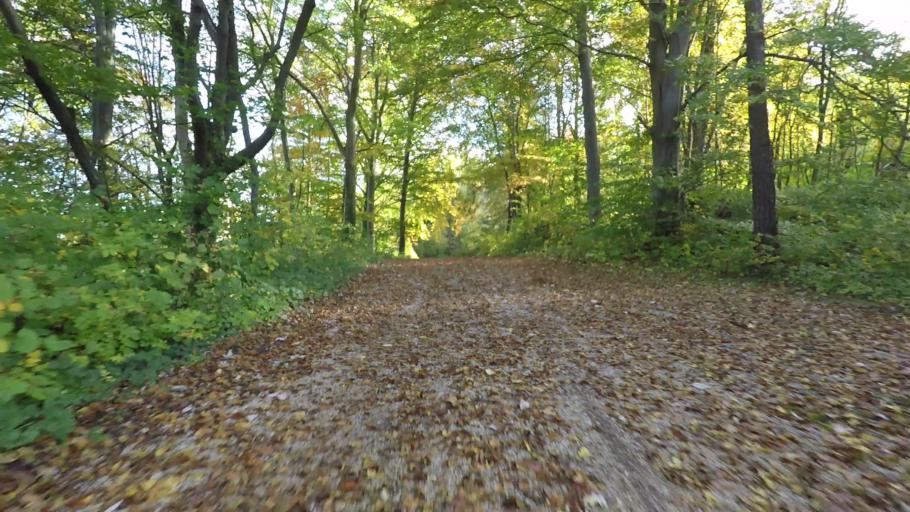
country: DE
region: Baden-Wuerttemberg
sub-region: Tuebingen Region
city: Pfullingen
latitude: 48.4486
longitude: 9.2297
